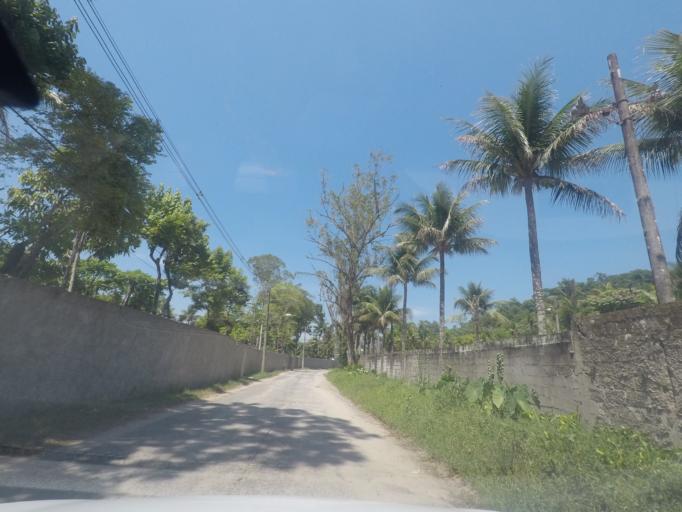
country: BR
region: Rio de Janeiro
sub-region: Nilopolis
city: Nilopolis
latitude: -22.9778
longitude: -43.4530
